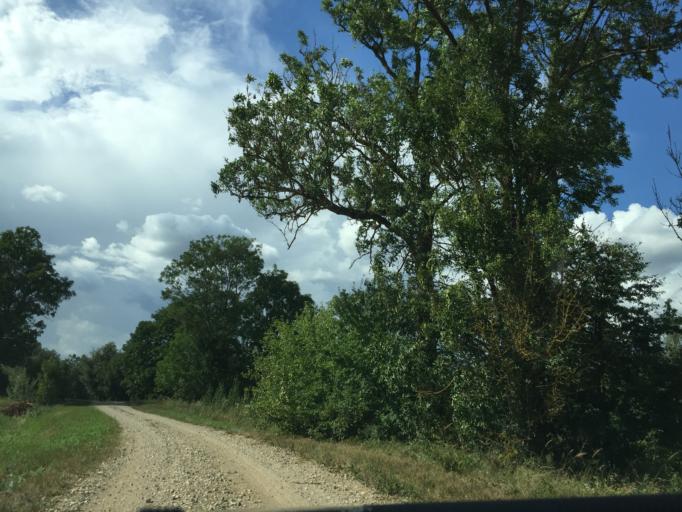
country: LT
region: Siauliu apskritis
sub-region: Joniskis
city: Joniskis
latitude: 56.3564
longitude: 23.5683
